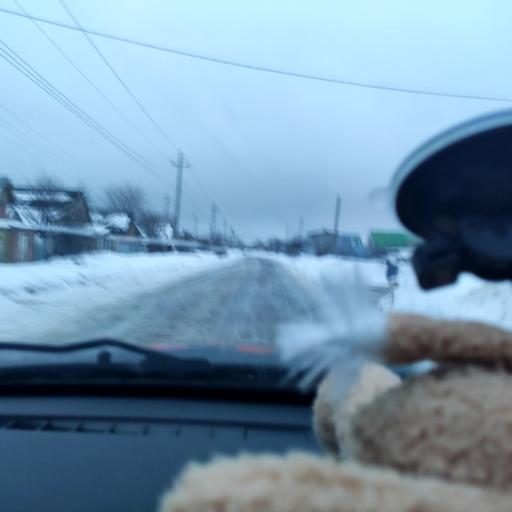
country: RU
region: Samara
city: Tol'yatti
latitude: 53.5740
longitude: 49.3243
